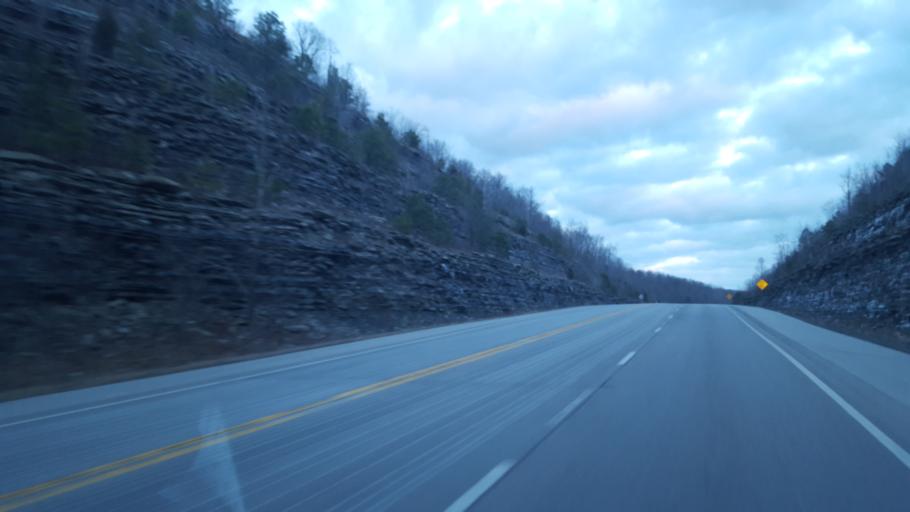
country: US
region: Kentucky
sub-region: Lewis County
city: Vanceburg
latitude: 38.5748
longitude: -83.3010
